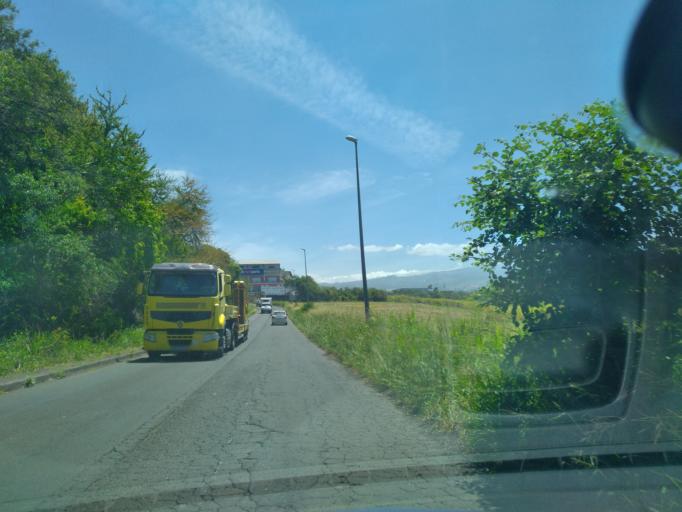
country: RE
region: Reunion
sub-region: Reunion
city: Saint-Pierre
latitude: -21.3237
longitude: 55.4479
